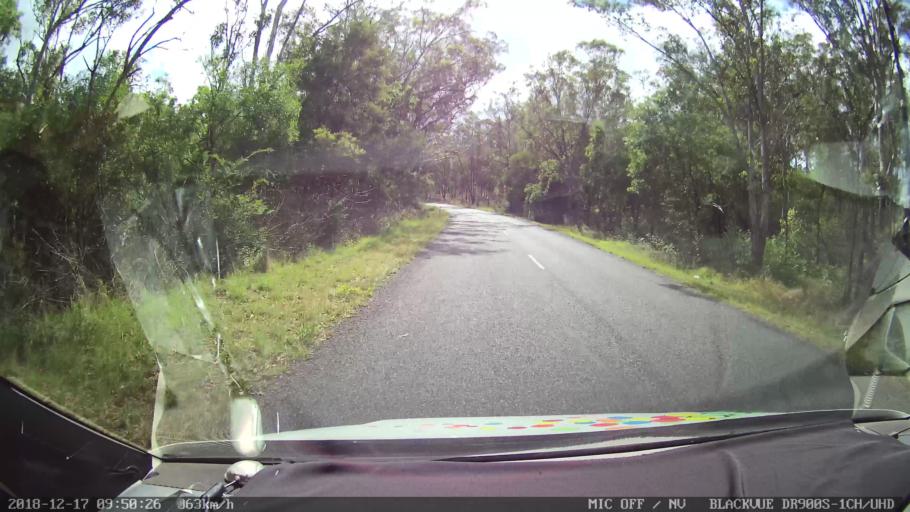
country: AU
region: New South Wales
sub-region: Tenterfield Municipality
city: Carrolls Creek
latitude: -28.9267
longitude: 152.3638
